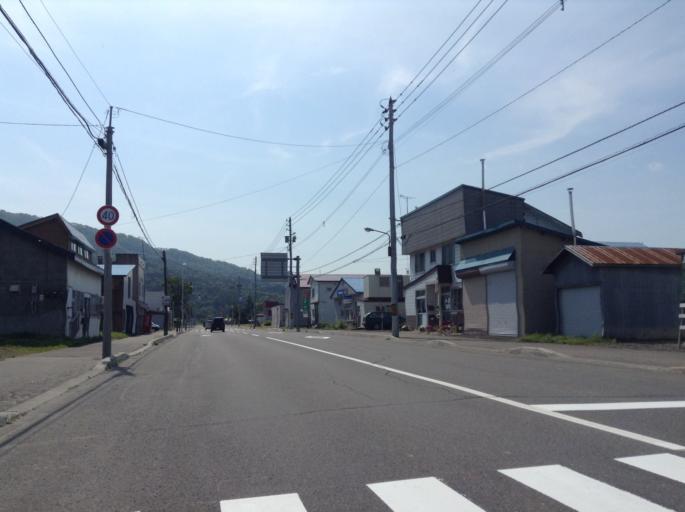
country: JP
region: Hokkaido
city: Nayoro
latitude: 44.7273
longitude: 142.2599
